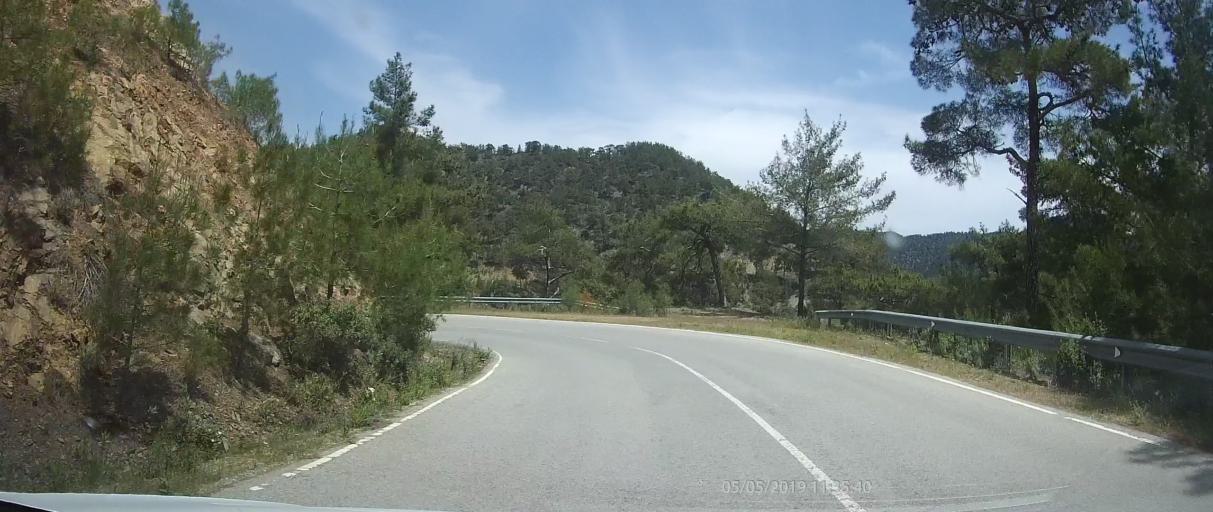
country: CY
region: Lefkosia
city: Kato Pyrgos
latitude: 34.9694
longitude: 32.6518
